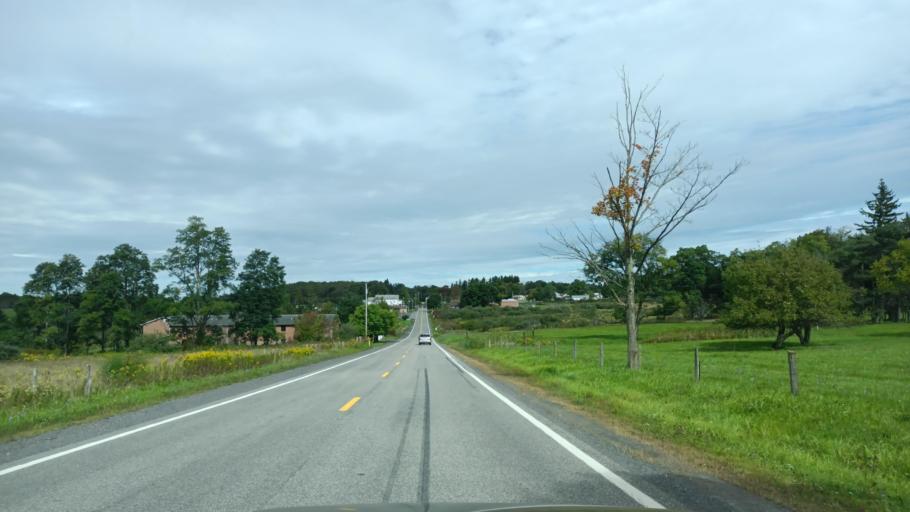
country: US
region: Maryland
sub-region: Garrett County
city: Mountain Lake Park
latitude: 39.2716
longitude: -79.2385
